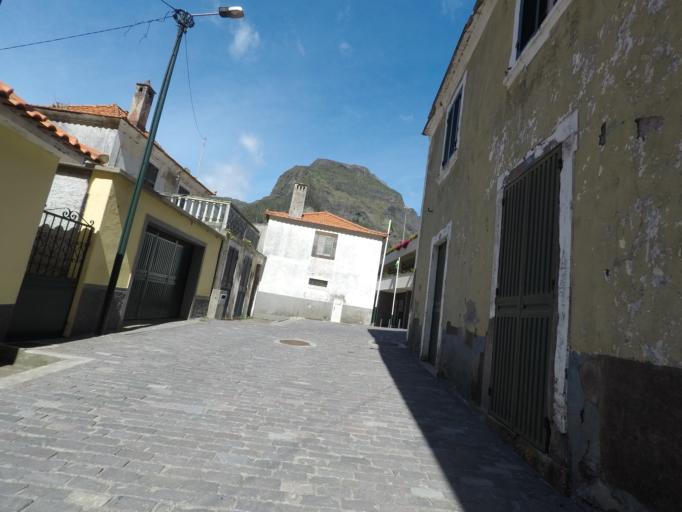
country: PT
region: Madeira
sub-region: Camara de Lobos
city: Curral das Freiras
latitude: 32.7200
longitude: -16.9652
